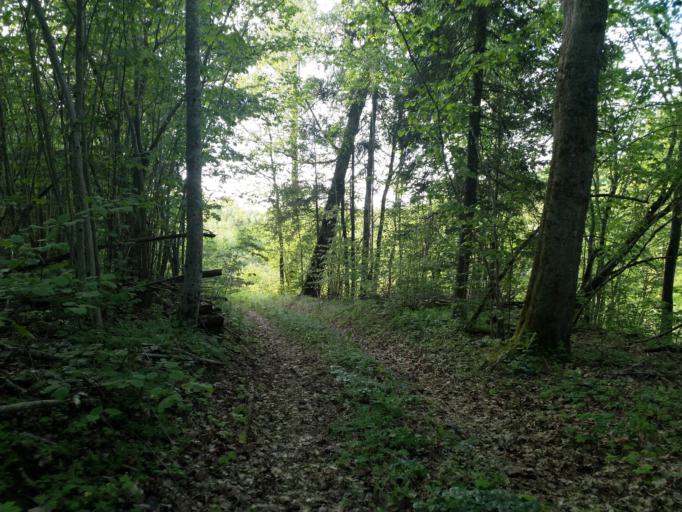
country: LV
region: Kuldigas Rajons
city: Kuldiga
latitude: 56.8553
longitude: 21.8677
